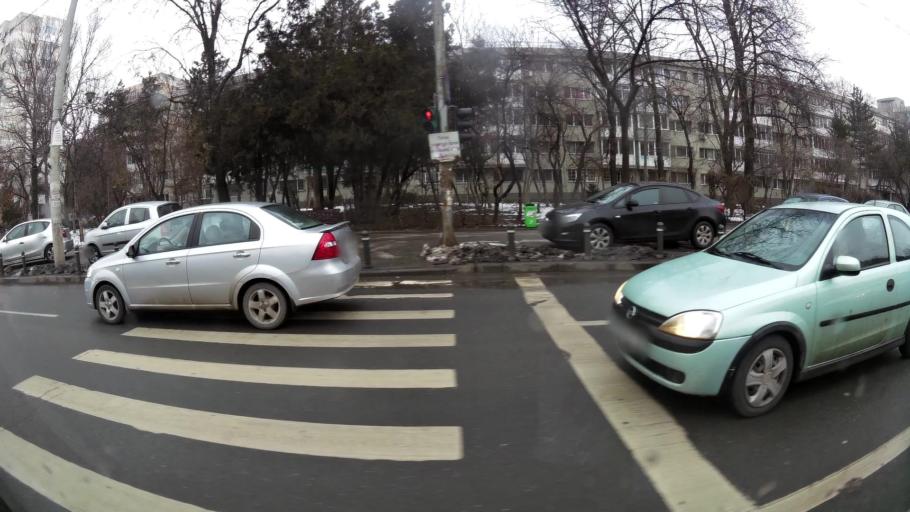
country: RO
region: Ilfov
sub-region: Comuna Chiajna
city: Rosu
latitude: 44.4249
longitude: 26.0340
